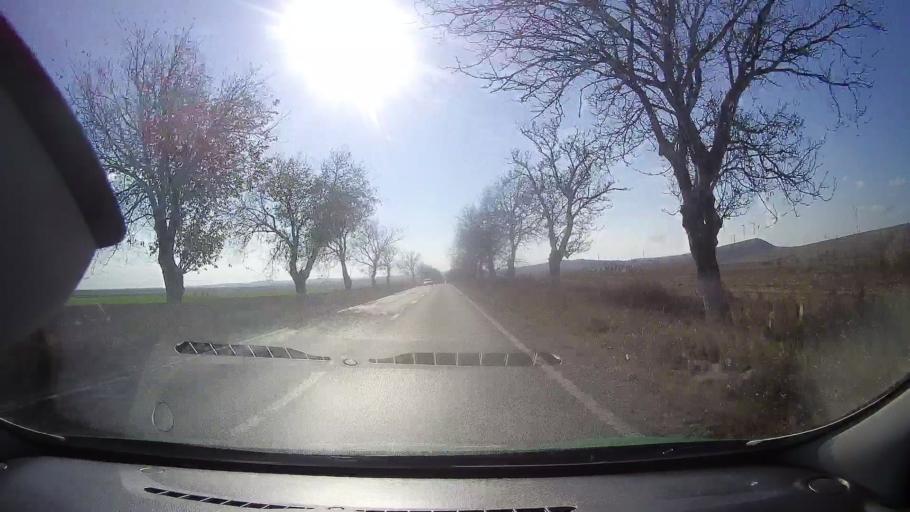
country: RO
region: Tulcea
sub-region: Comuna Ceamurlia de Jos
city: Ceamurlia de Jos
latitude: 44.7873
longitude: 28.6896
